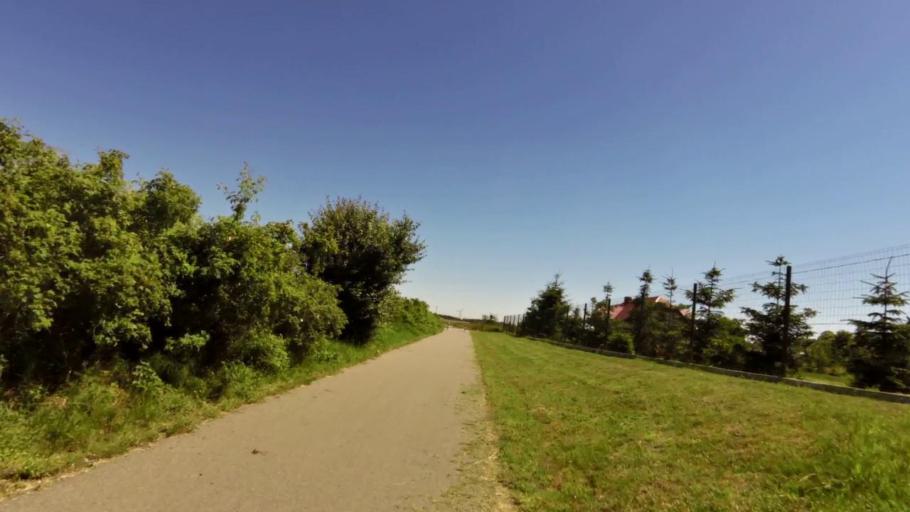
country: PL
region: West Pomeranian Voivodeship
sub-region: Powiat kolobrzeski
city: Goscino
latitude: 54.0909
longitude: 15.5817
